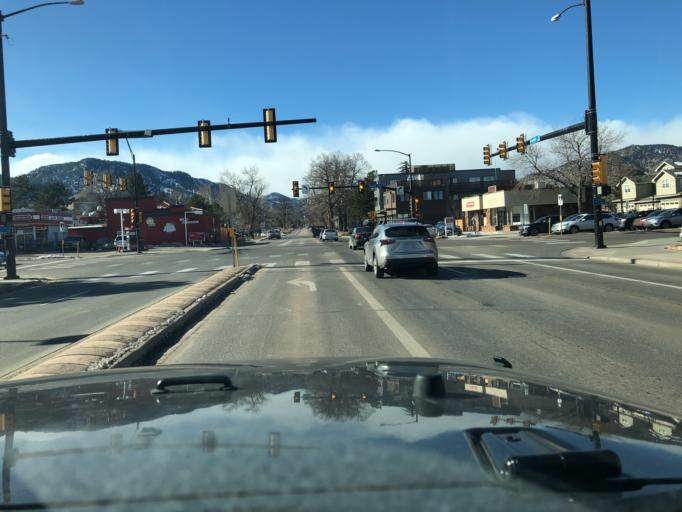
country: US
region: Colorado
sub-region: Boulder County
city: Boulder
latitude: 40.0147
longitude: -105.2625
